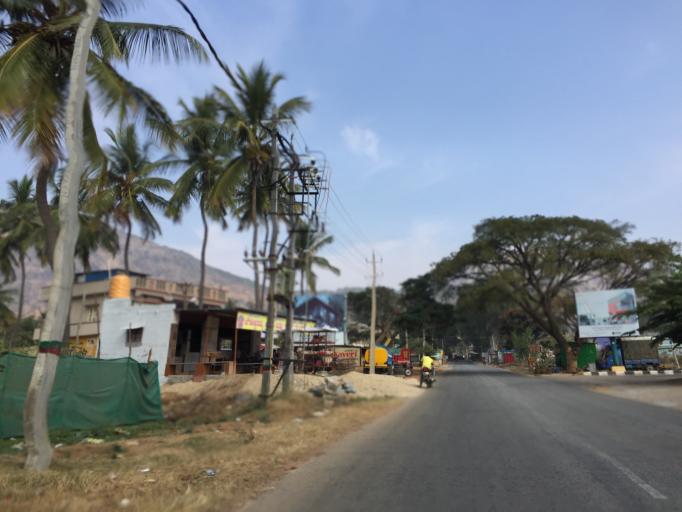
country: IN
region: Karnataka
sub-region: Chikkaballapur
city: Chik Ballapur
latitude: 13.3465
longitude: 77.6869
